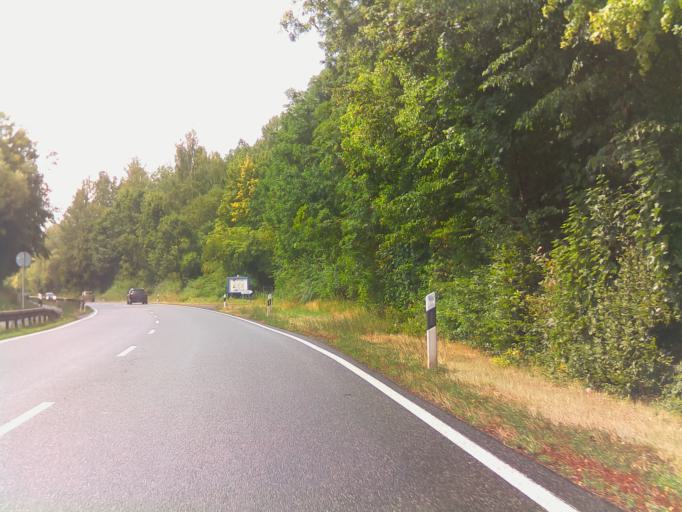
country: DE
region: Hesse
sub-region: Regierungsbezirk Giessen
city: Lauterbach
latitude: 50.6396
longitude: 9.4219
